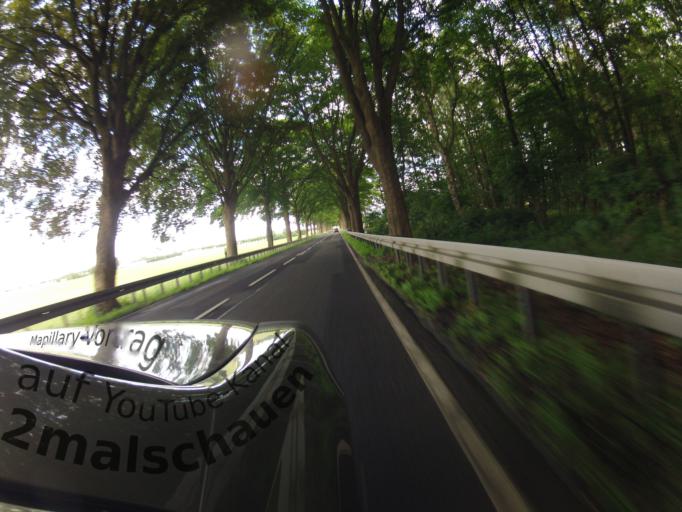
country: DE
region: Mecklenburg-Vorpommern
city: Usedom
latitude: 53.9049
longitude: 14.0389
